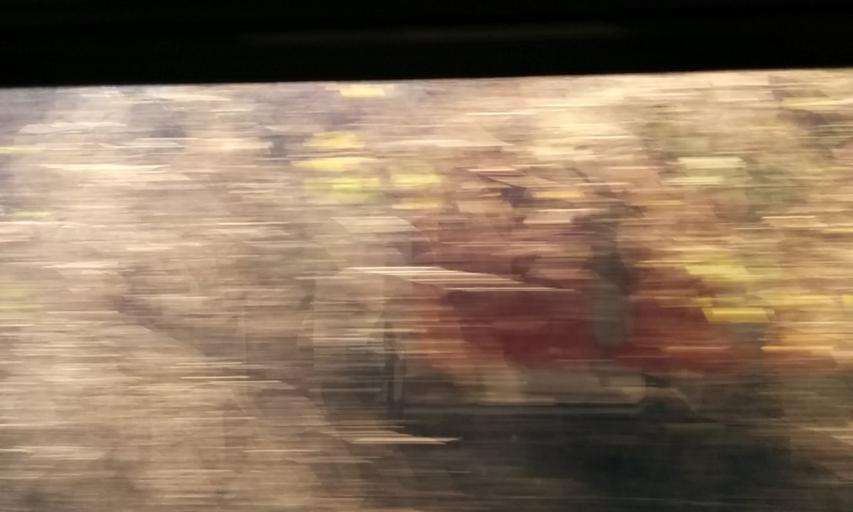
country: JP
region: Nagano
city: Iida
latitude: 35.7012
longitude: 137.6974
